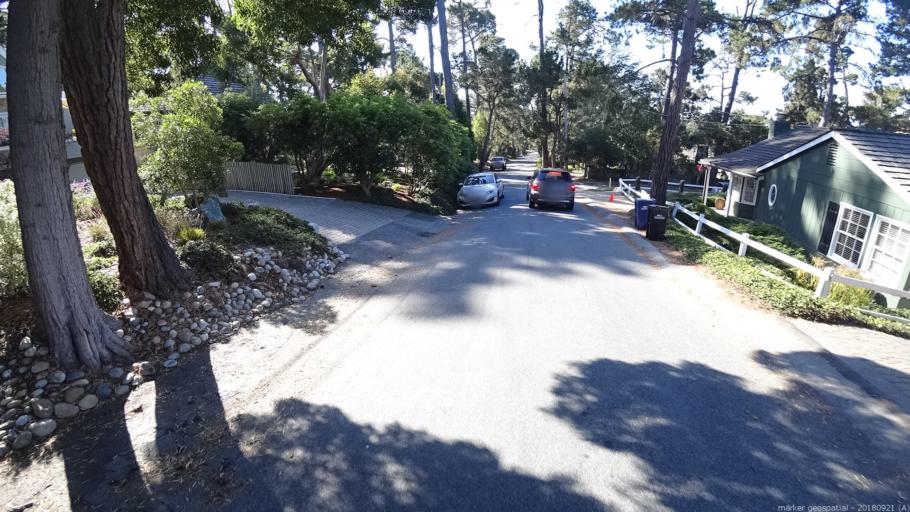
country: US
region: California
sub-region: Monterey County
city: Carmel-by-the-Sea
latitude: 36.5634
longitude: -121.9218
